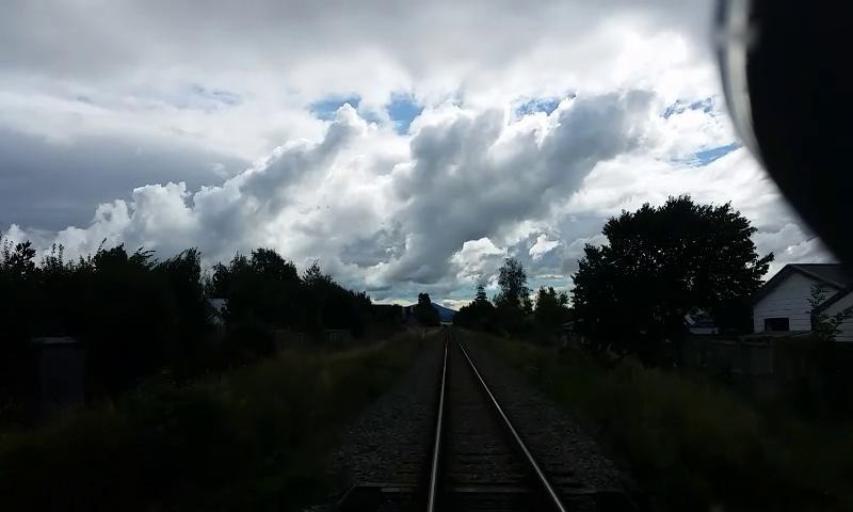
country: NZ
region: Canterbury
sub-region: Waimakariri District
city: Woodend
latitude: -43.3094
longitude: 172.5999
